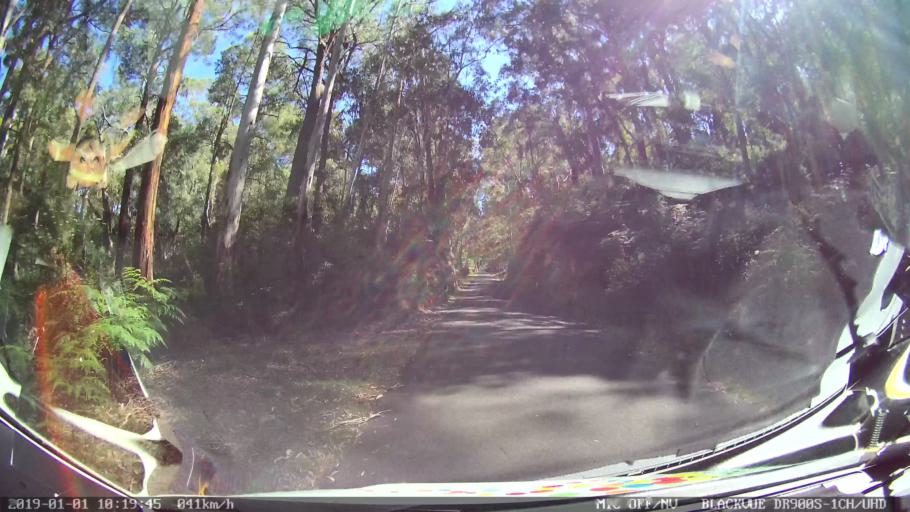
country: AU
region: New South Wales
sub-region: Snowy River
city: Jindabyne
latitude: -36.0825
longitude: 148.1861
